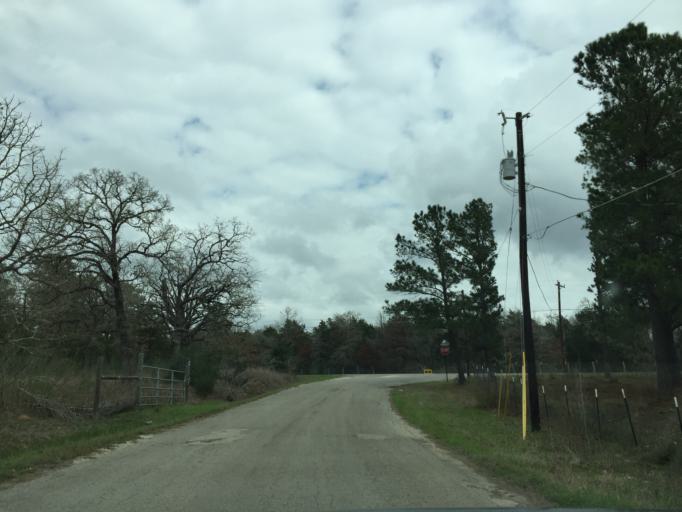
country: US
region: Texas
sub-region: Bastrop County
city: Bastrop
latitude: 30.1300
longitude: -97.2856
